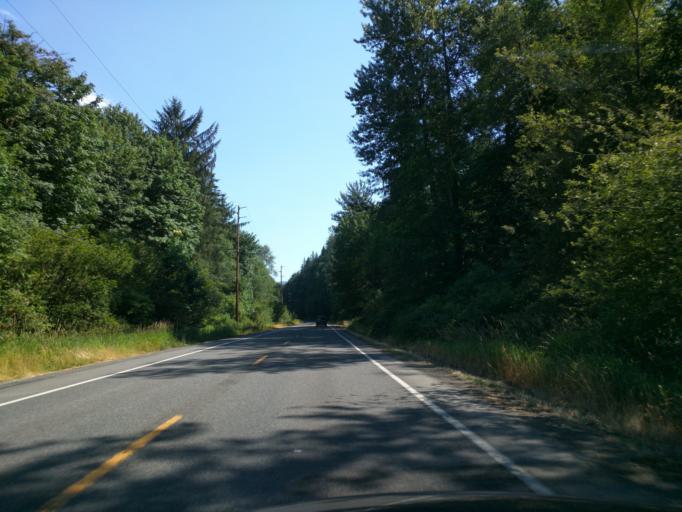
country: US
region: Washington
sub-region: Whatcom County
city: Peaceful Valley
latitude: 48.8771
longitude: -122.1572
